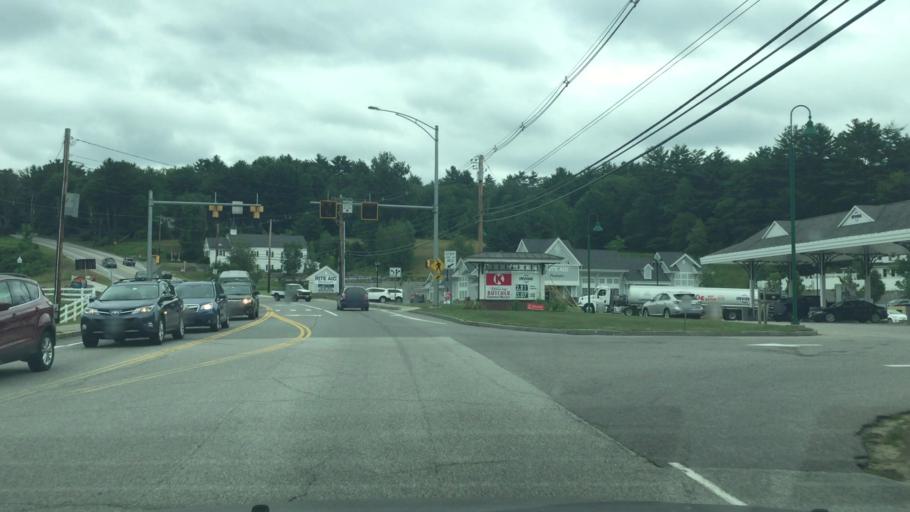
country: US
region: New Hampshire
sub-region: Belknap County
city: Meredith
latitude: 43.6615
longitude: -71.4944
